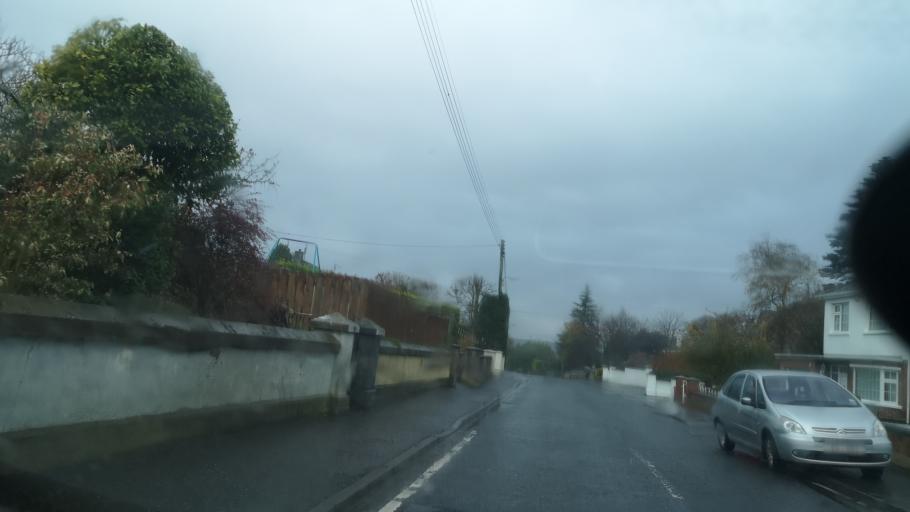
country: GB
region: Northern Ireland
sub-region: Newry and Mourne District
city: Newry
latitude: 54.1794
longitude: -6.3262
